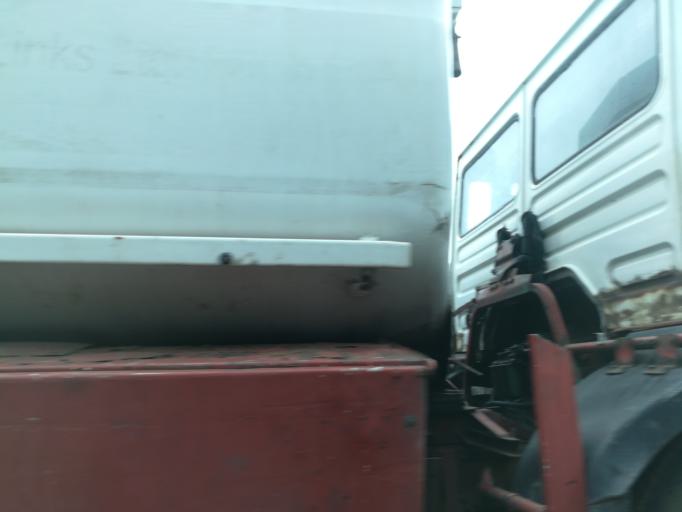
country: NG
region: Lagos
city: Lagos
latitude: 6.4333
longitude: 3.4127
